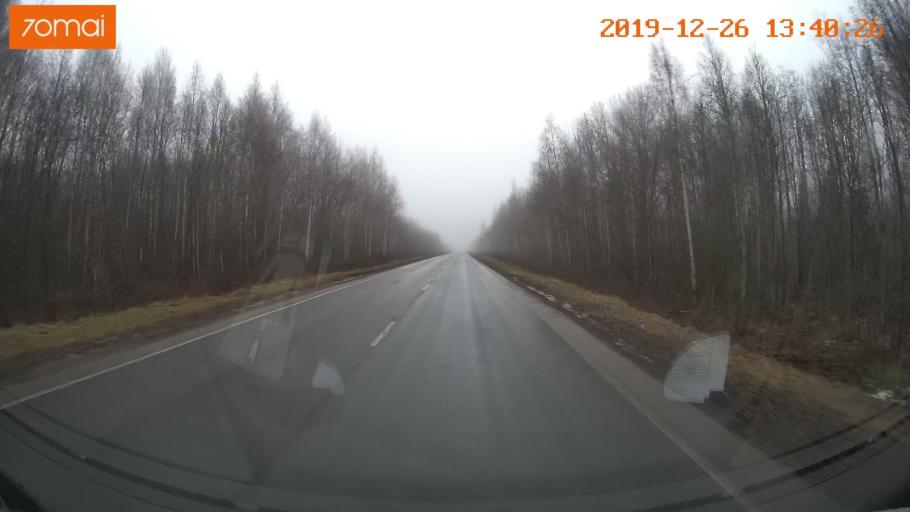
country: RU
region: Vologda
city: Sheksna
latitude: 58.7425
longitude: 38.4295
